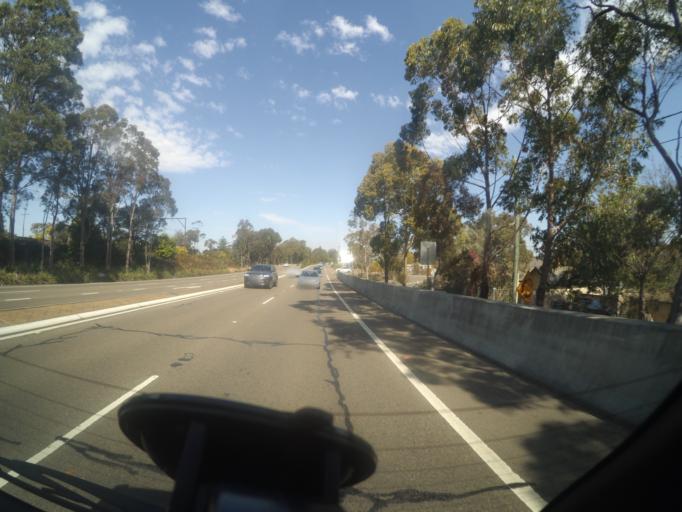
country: AU
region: New South Wales
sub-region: Blue Mountains Municipality
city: Blaxland
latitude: -33.7267
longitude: 150.6054
